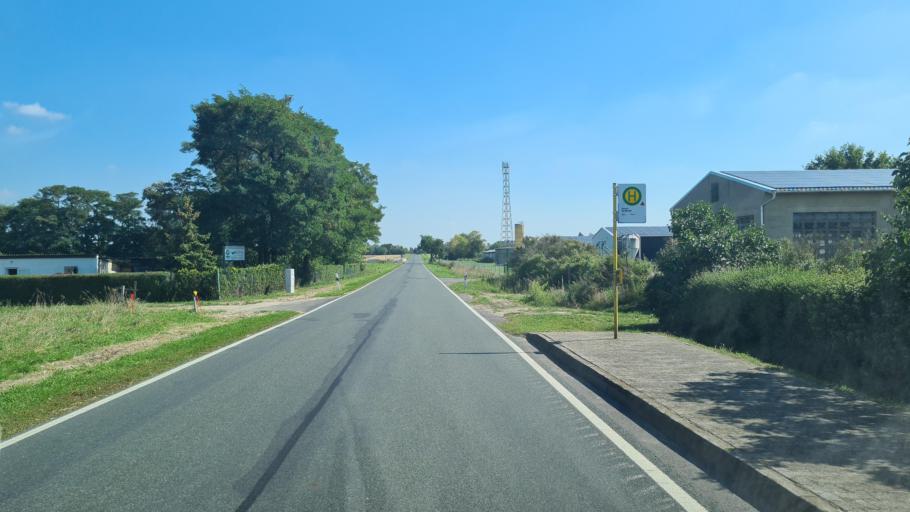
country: DE
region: Brandenburg
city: Friesack
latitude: 52.7320
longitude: 12.6138
